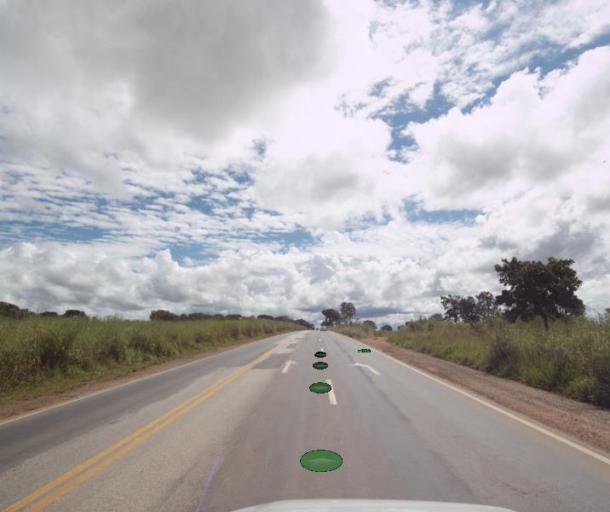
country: BR
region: Goias
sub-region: Uruacu
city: Uruacu
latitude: -14.3430
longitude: -49.1565
